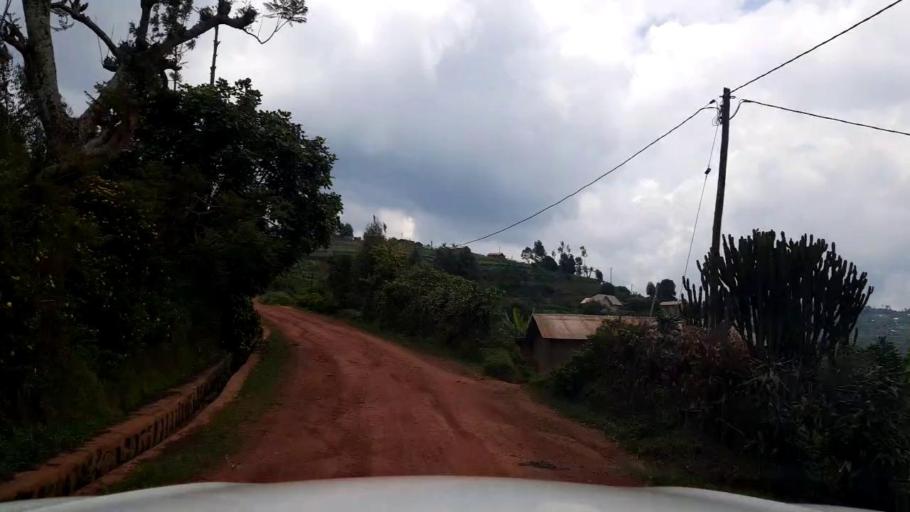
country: RW
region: Northern Province
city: Byumba
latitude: -1.4891
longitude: 29.9094
